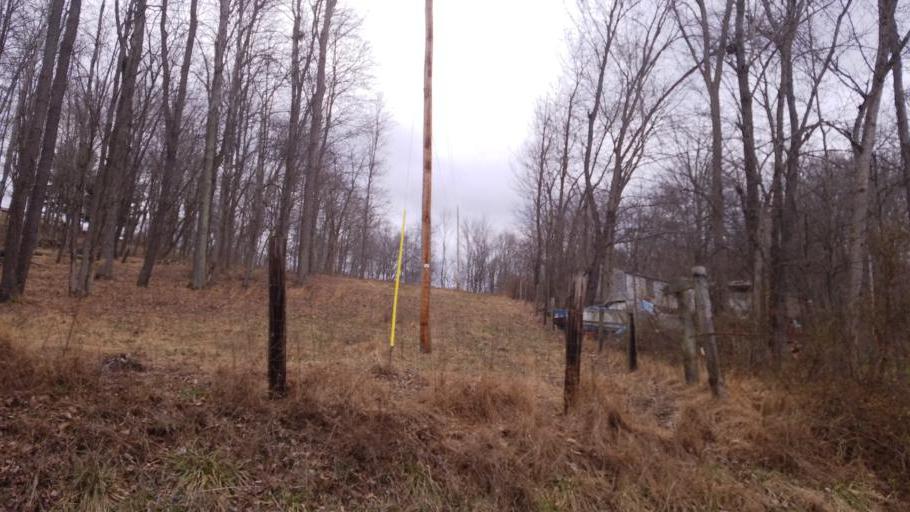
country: US
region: Ohio
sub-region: Muskingum County
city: Frazeysburg
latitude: 40.1148
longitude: -82.2077
